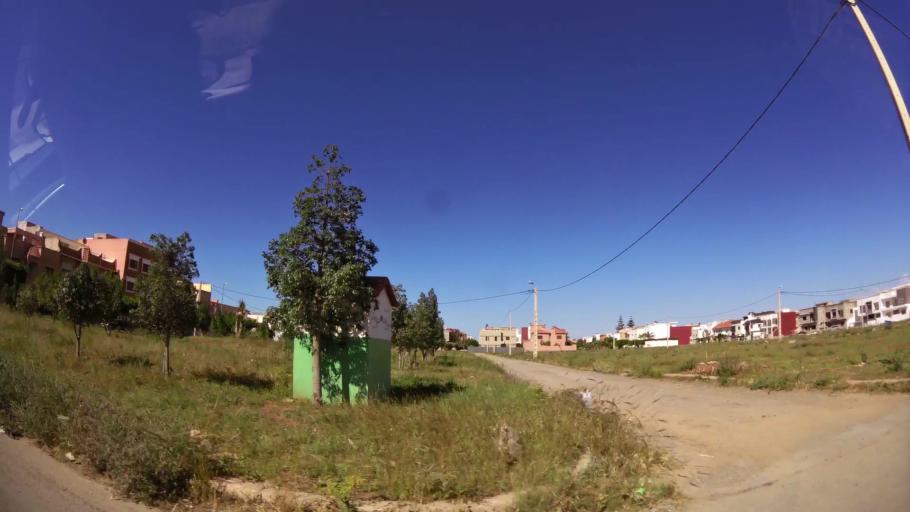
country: MA
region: Oriental
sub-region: Berkane-Taourirt
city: Berkane
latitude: 34.9429
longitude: -2.3368
